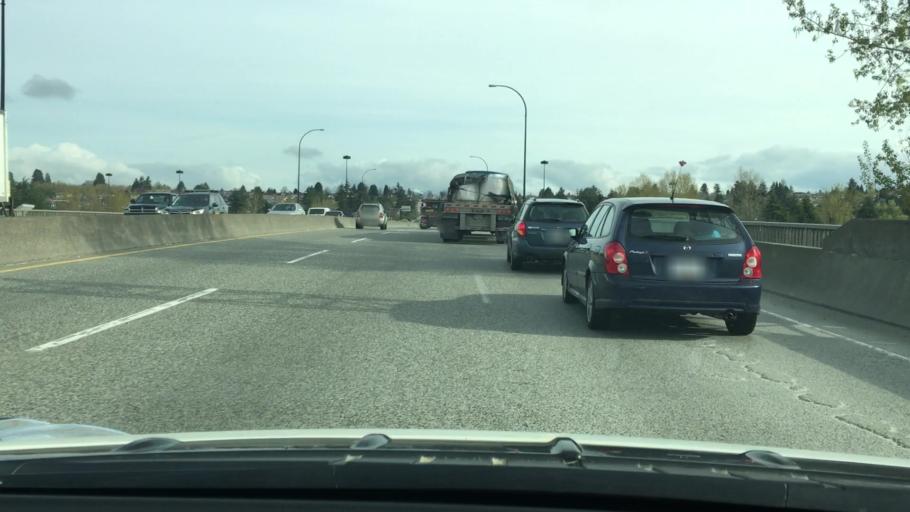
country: CA
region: British Columbia
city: Vancouver
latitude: 49.2075
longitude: -123.0772
